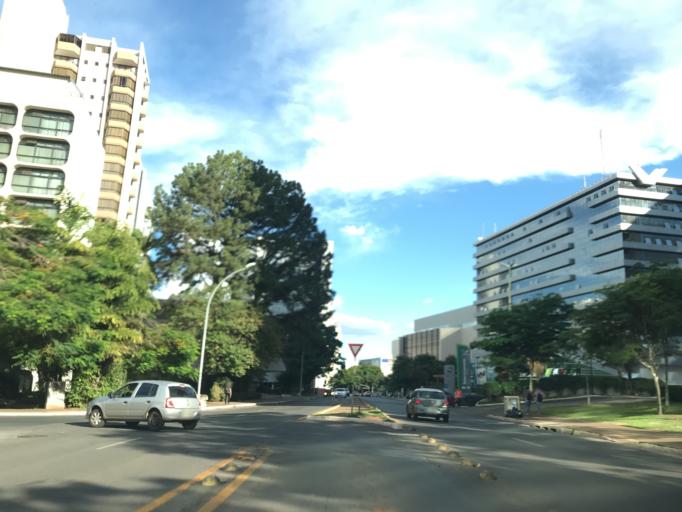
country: BR
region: Federal District
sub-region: Brasilia
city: Brasilia
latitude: -15.7941
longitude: -47.8932
